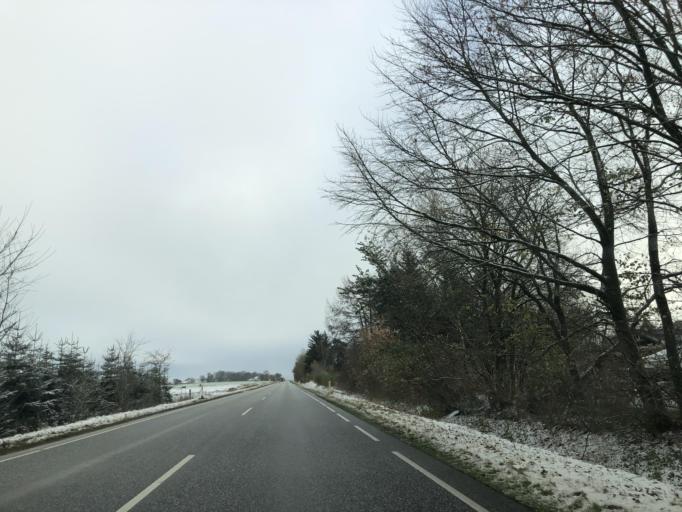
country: DK
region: Central Jutland
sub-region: Horsens Kommune
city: Braedstrup
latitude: 55.8932
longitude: 9.6518
